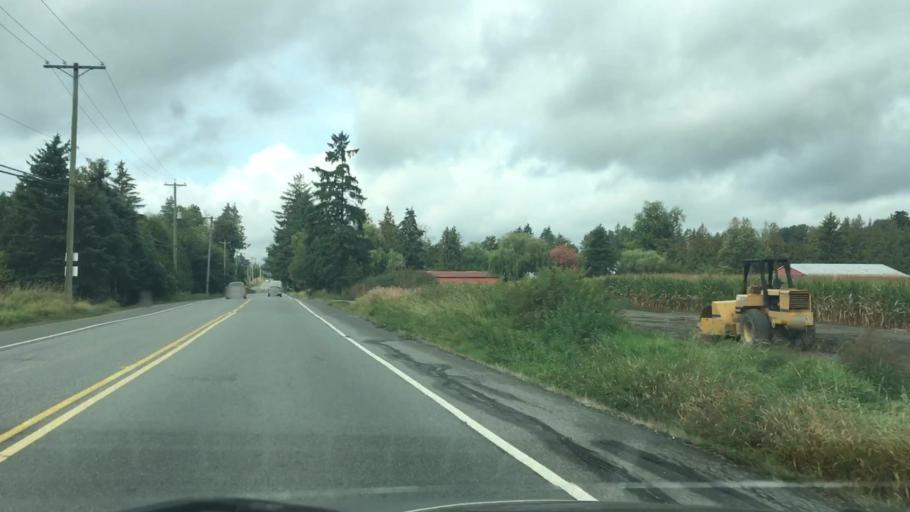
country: CA
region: British Columbia
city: Langley
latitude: 49.1041
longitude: -122.5826
